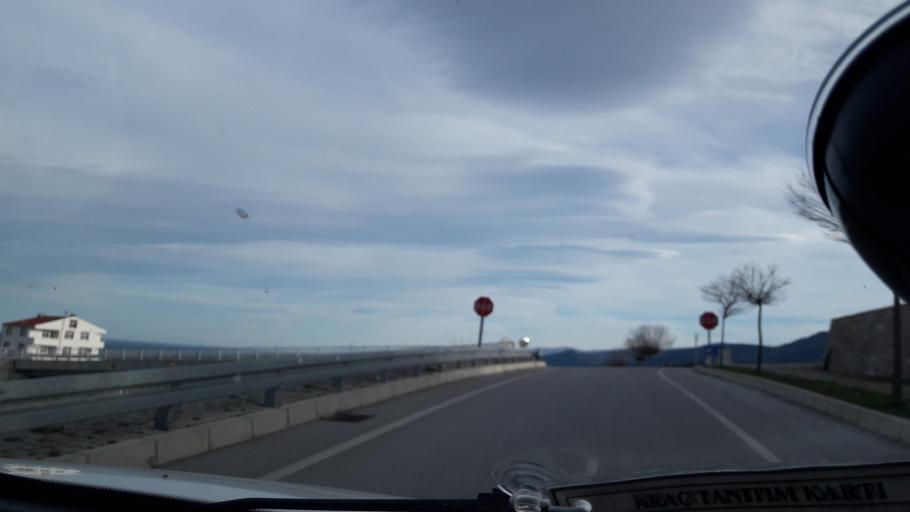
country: TR
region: Sinop
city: Gerze
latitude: 41.8020
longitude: 35.1774
